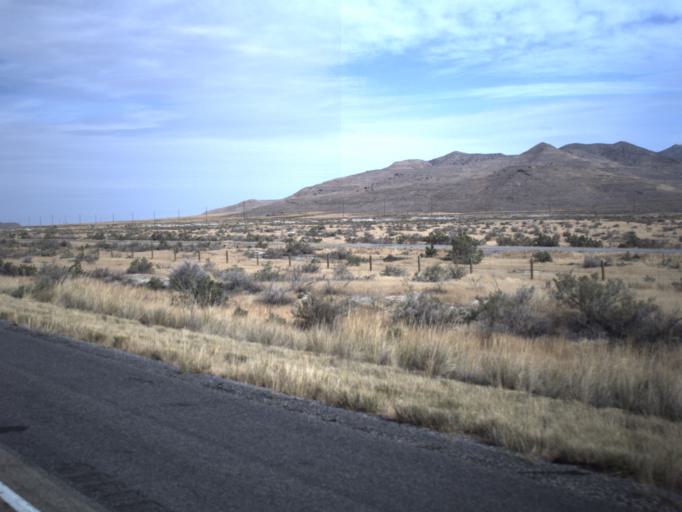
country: US
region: Utah
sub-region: Tooele County
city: Grantsville
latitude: 40.7839
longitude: -112.8196
